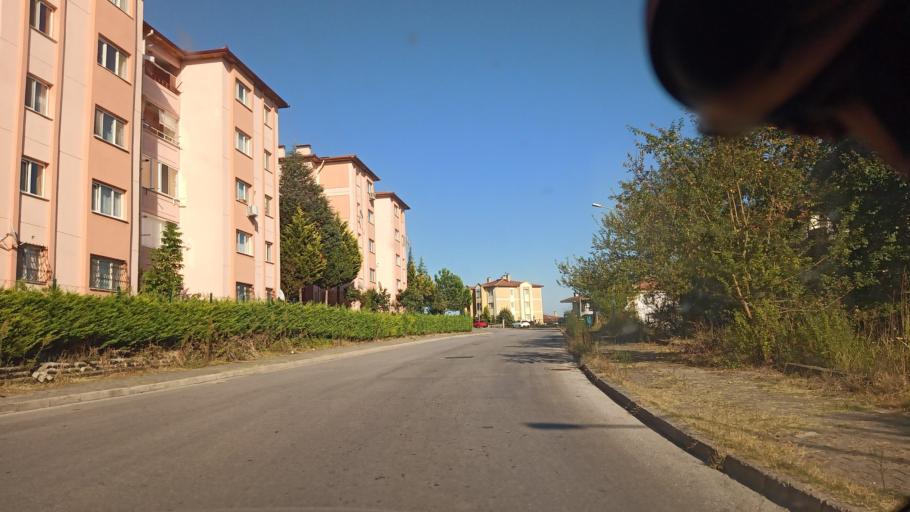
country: TR
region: Sakarya
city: Kazimpasa
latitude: 40.8556
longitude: 30.2926
